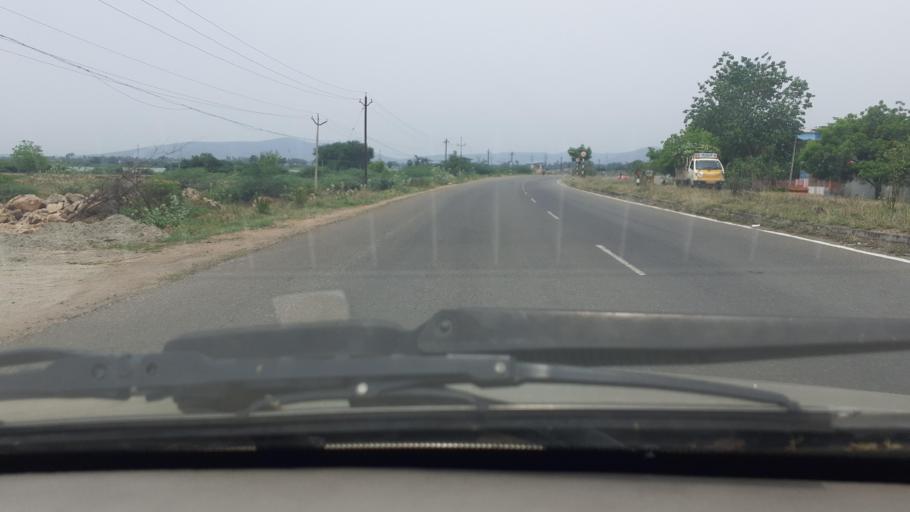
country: IN
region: Tamil Nadu
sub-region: Tirunelveli Kattabo
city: Tirunelveli
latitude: 8.7112
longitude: 77.8059
